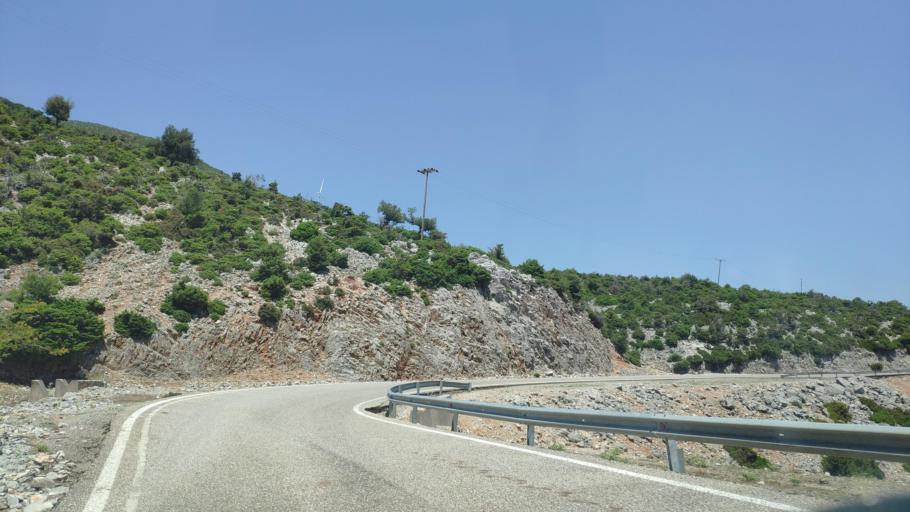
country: GR
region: West Greece
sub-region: Nomos Aitolias kai Akarnanias
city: Krikellos
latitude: 39.0545
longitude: 21.3837
